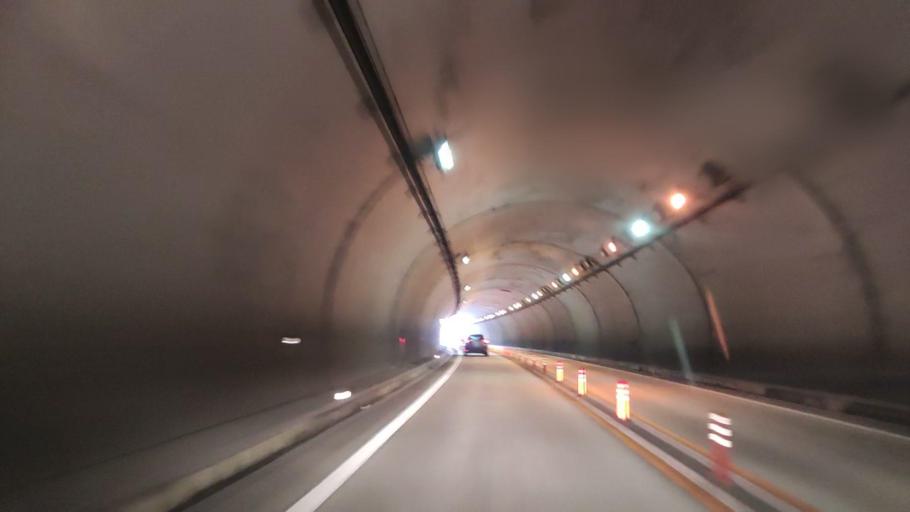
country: JP
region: Hiroshima
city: Innoshima
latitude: 34.2945
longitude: 133.1441
